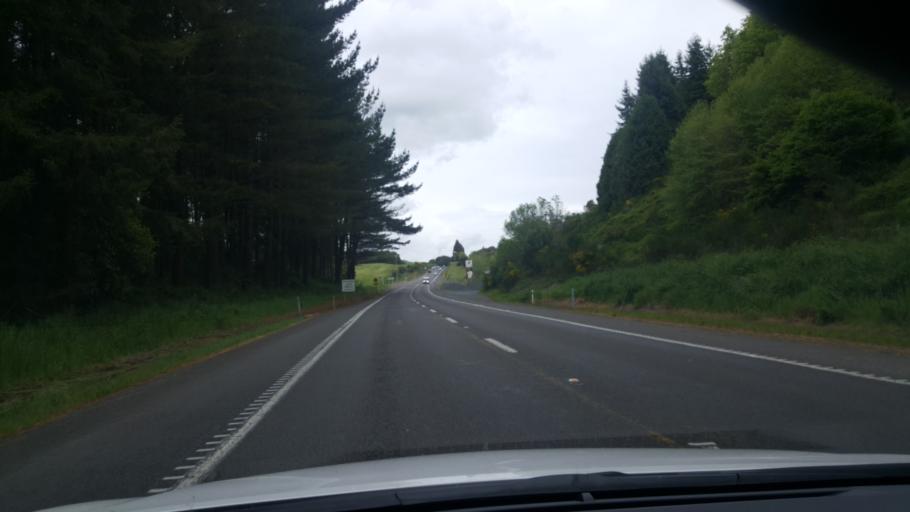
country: NZ
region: Bay of Plenty
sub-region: Rotorua District
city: Rotorua
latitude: -38.2434
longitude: 176.3087
